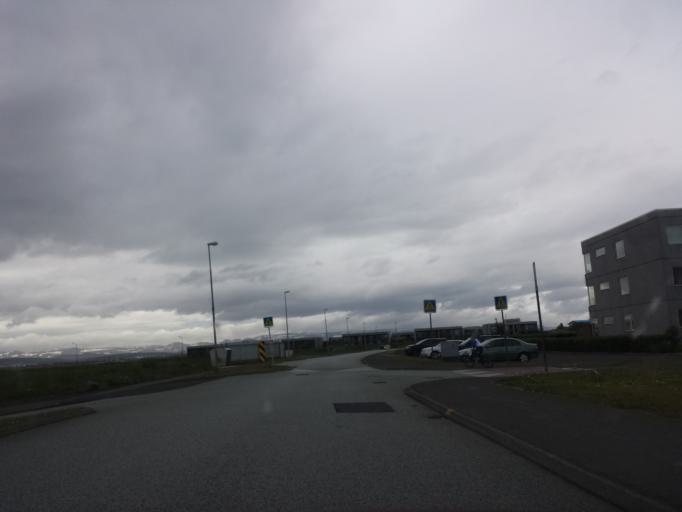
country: IS
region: Capital Region
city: Alftanes
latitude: 64.1029
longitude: -22.0189
